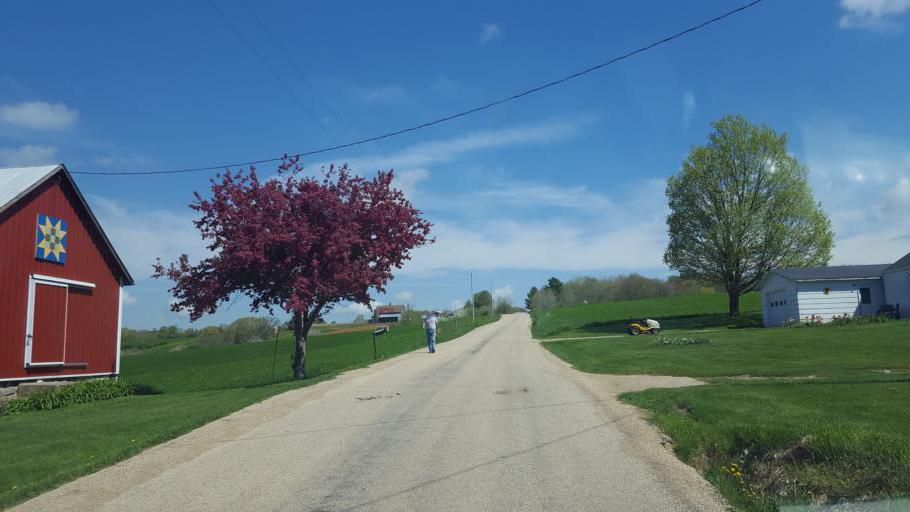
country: US
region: Wisconsin
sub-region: Juneau County
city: Elroy
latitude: 43.7141
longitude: -90.3011
